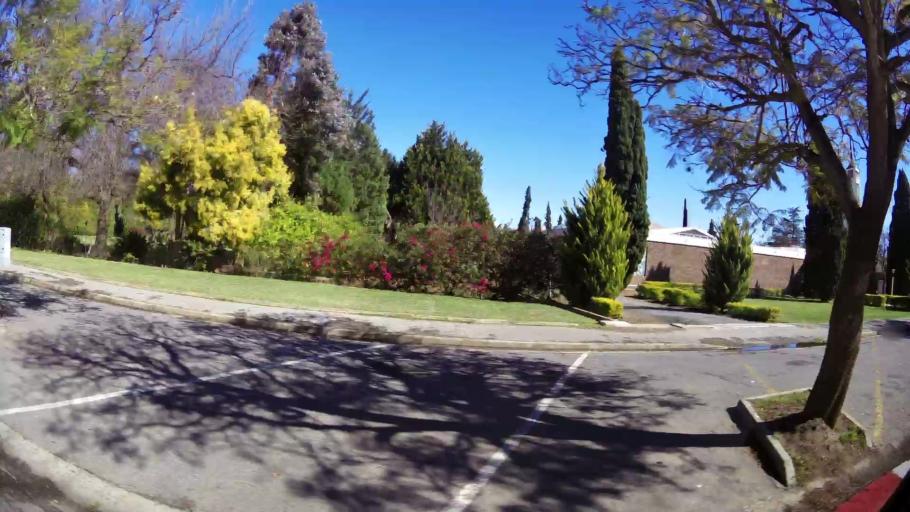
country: ZA
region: Western Cape
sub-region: Cape Winelands District Municipality
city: Ashton
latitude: -33.8047
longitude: 19.8926
